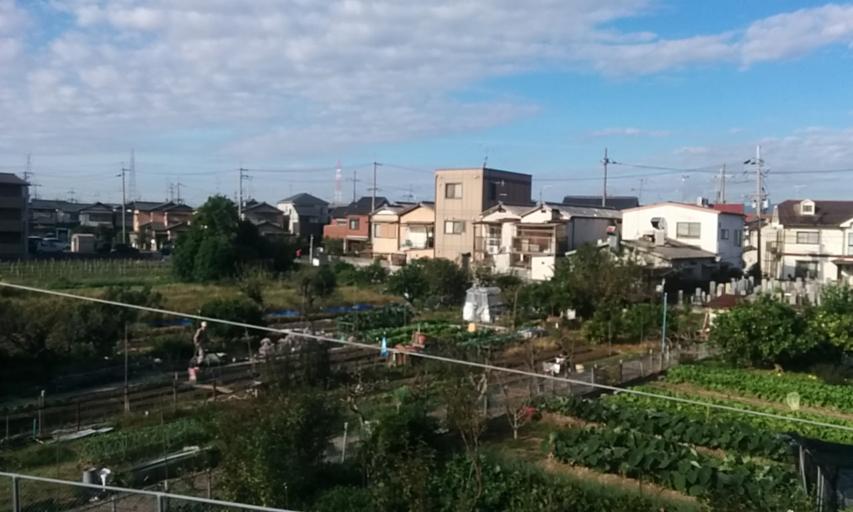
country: JP
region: Kyoto
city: Uji
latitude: 34.9225
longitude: 135.7669
